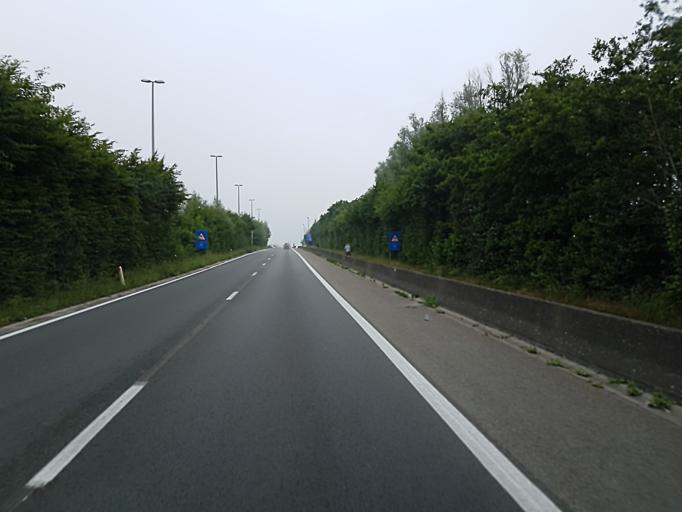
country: FR
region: Nord-Pas-de-Calais
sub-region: Departement du Nord
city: Halluin
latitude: 50.7923
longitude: 3.1381
